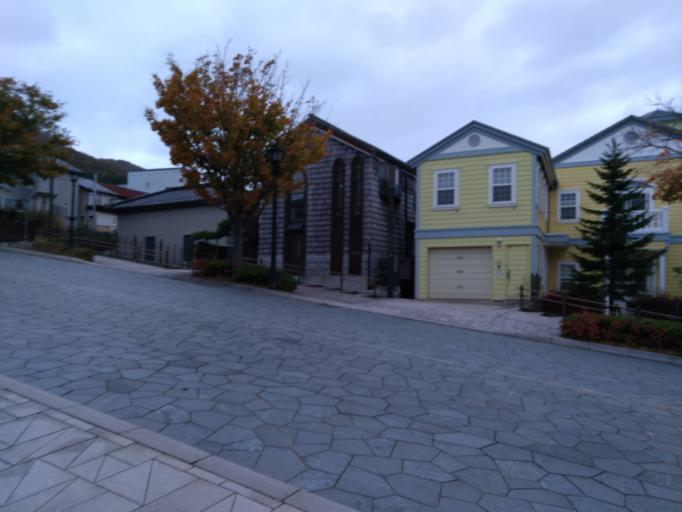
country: JP
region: Hokkaido
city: Hakodate
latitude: 41.7649
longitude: 140.7130
